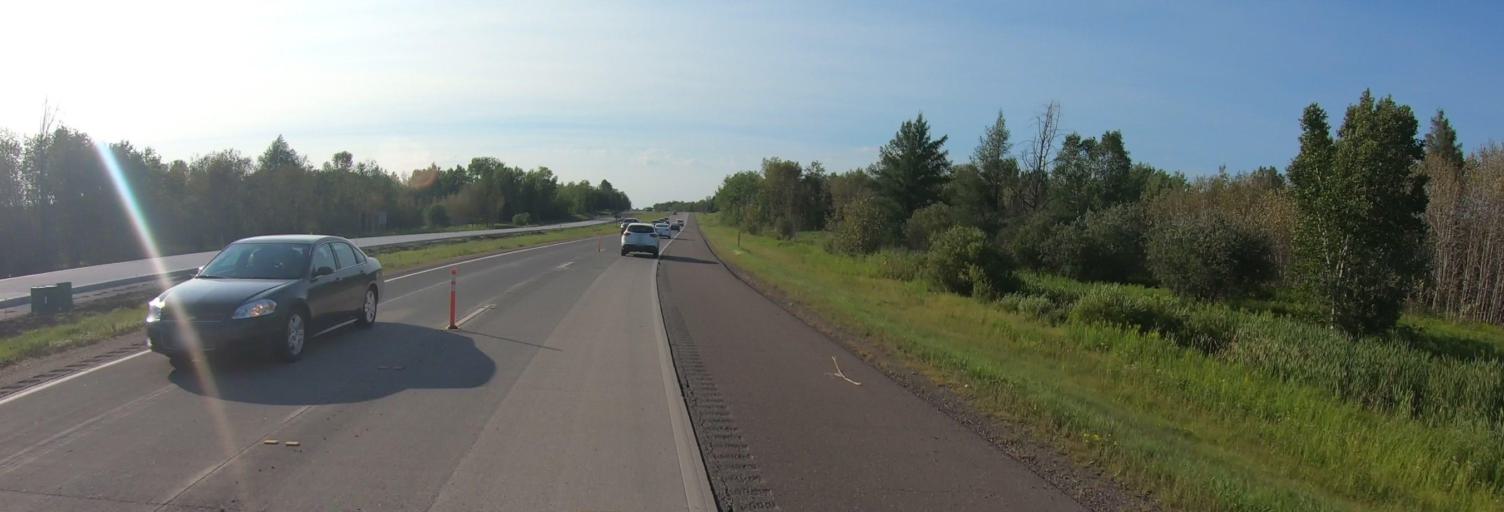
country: US
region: Minnesota
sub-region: Carlton County
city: Cloquet
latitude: 46.9244
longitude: -92.4131
